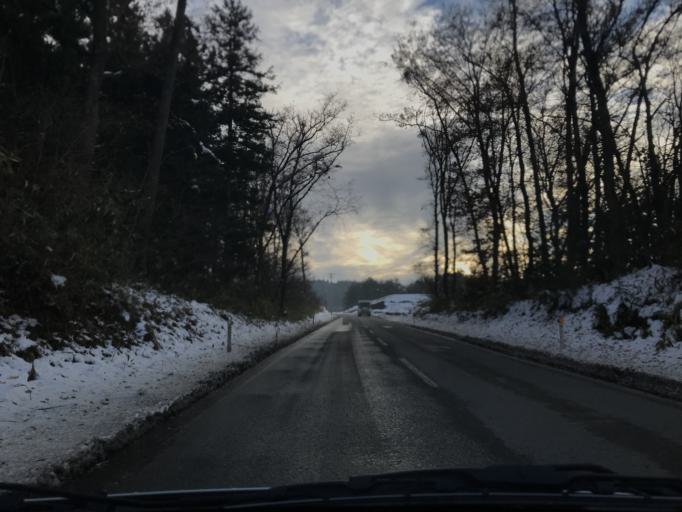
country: JP
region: Iwate
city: Mizusawa
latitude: 39.0554
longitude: 141.0838
